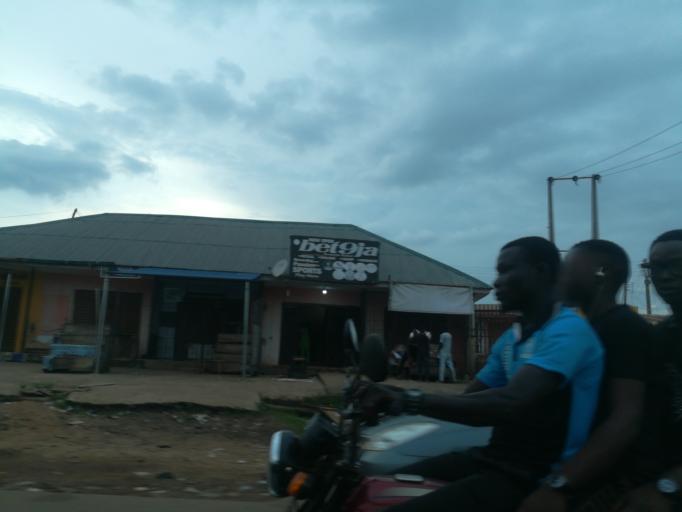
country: NG
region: Oyo
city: Ibadan
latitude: 7.4361
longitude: 3.9099
